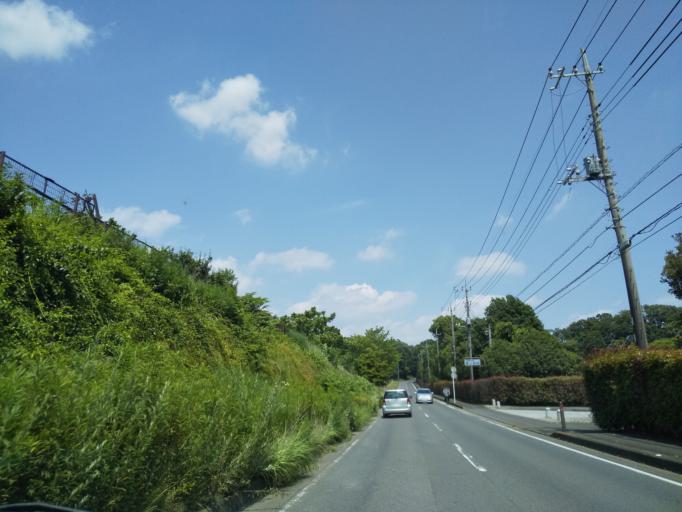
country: JP
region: Kanagawa
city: Zama
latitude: 35.5191
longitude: 139.3906
